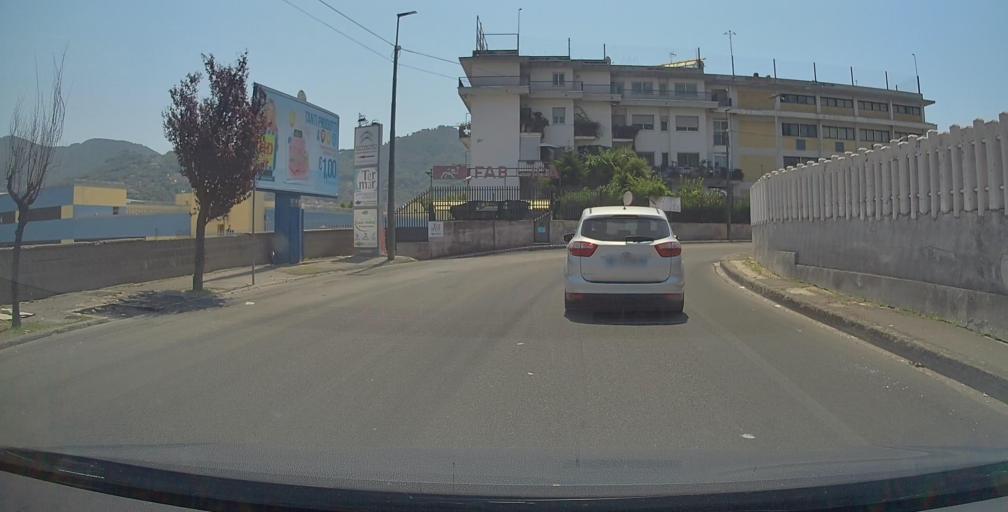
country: IT
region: Campania
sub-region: Provincia di Salerno
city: Cava De Tirreni
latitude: 40.7131
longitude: 14.6997
